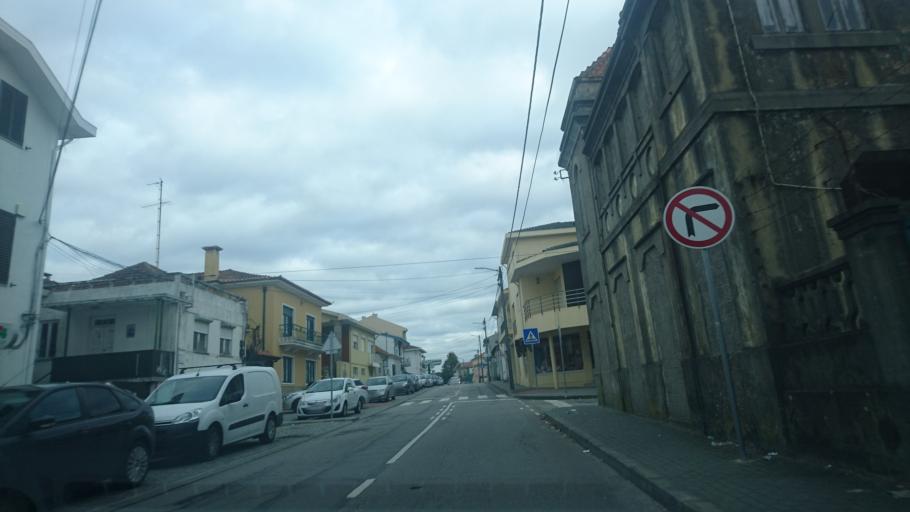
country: PT
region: Aveiro
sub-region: Santa Maria da Feira
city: Pacos de Brandao
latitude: 40.9735
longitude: -8.5825
